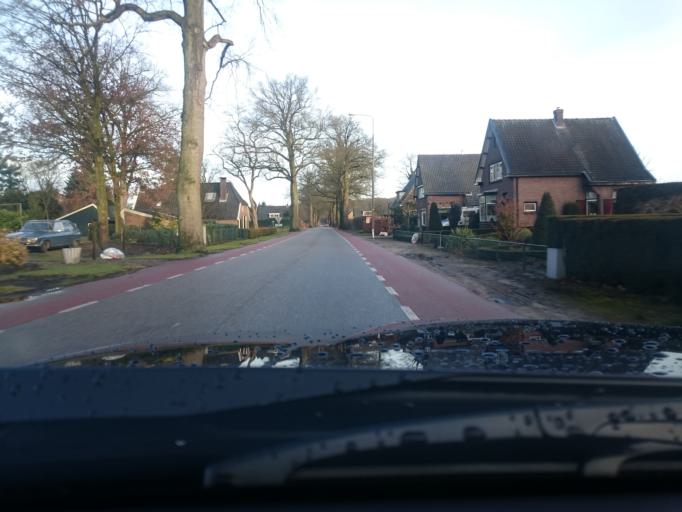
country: NL
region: Gelderland
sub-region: Gemeente Voorst
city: Voorst
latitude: 52.1848
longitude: 6.1345
